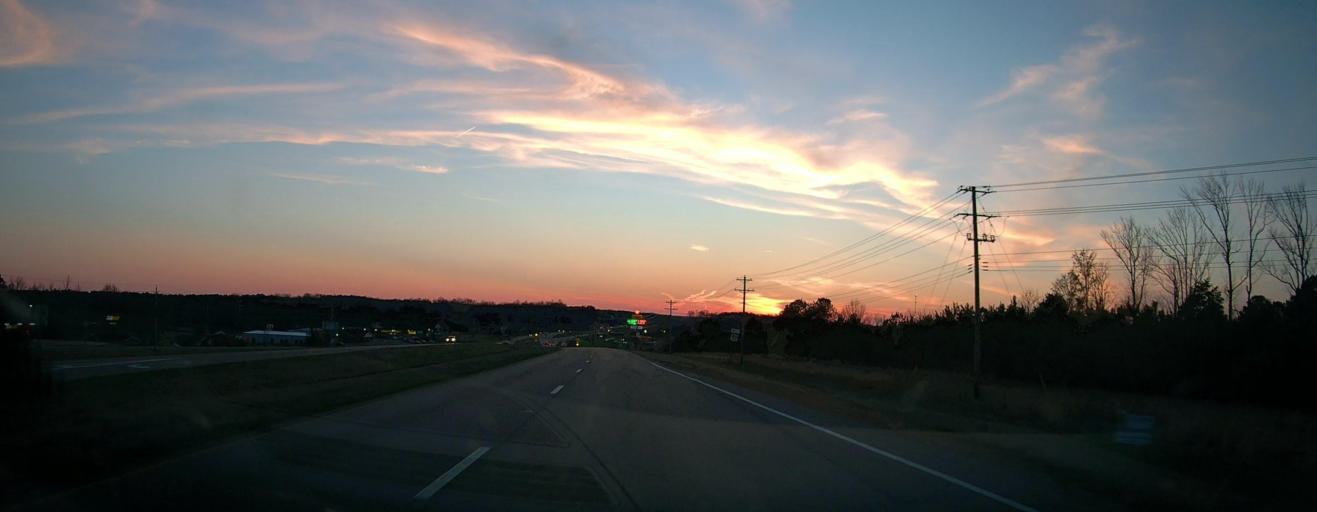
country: US
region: Mississippi
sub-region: Tippah County
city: Ripley
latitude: 34.9525
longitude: -88.9040
